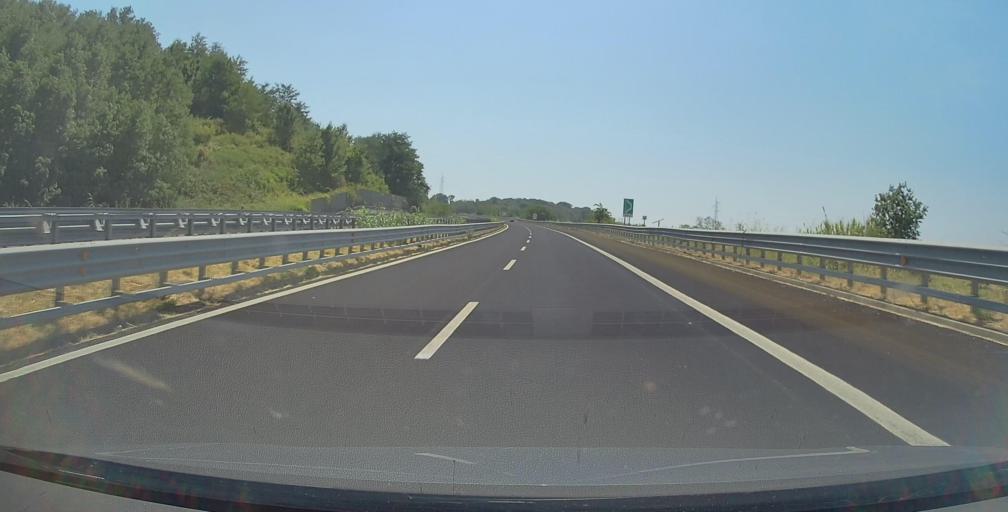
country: IT
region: Calabria
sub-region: Provincia di Reggio Calabria
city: Rosarno
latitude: 38.4987
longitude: 16.0205
